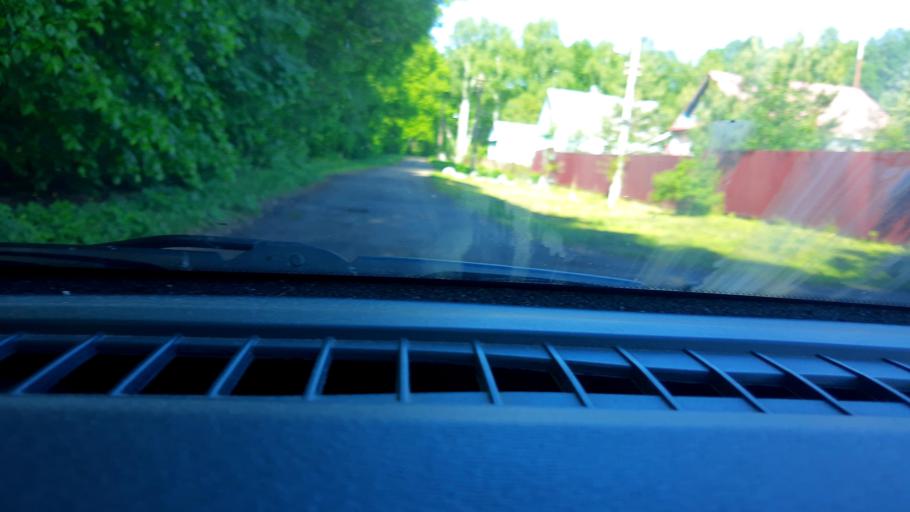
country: RU
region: Nizjnij Novgorod
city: Afonino
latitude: 56.1975
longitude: 44.0340
